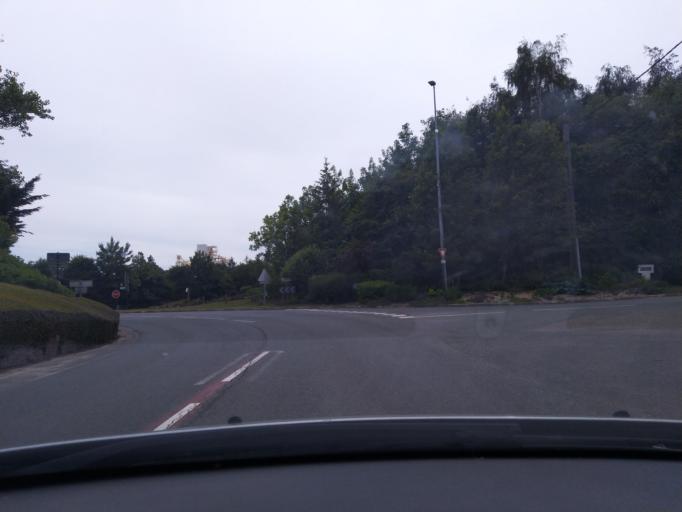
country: FR
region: Nord-Pas-de-Calais
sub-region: Departement du Pas-de-Calais
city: Ferques
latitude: 50.8296
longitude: 1.7556
